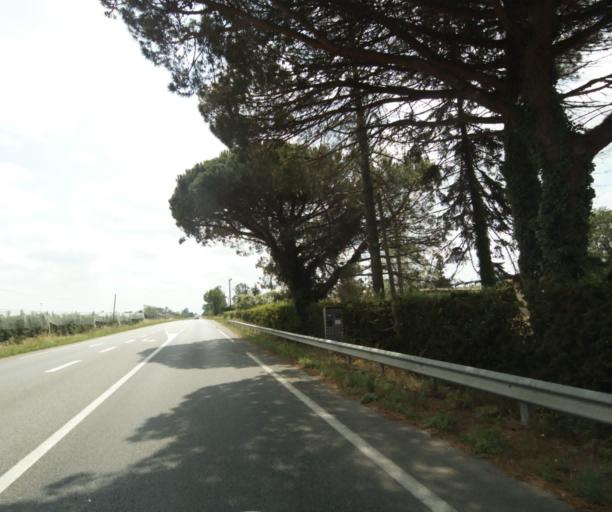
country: FR
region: Midi-Pyrenees
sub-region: Departement du Tarn-et-Garonne
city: Albias
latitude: 44.0668
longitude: 1.4173
